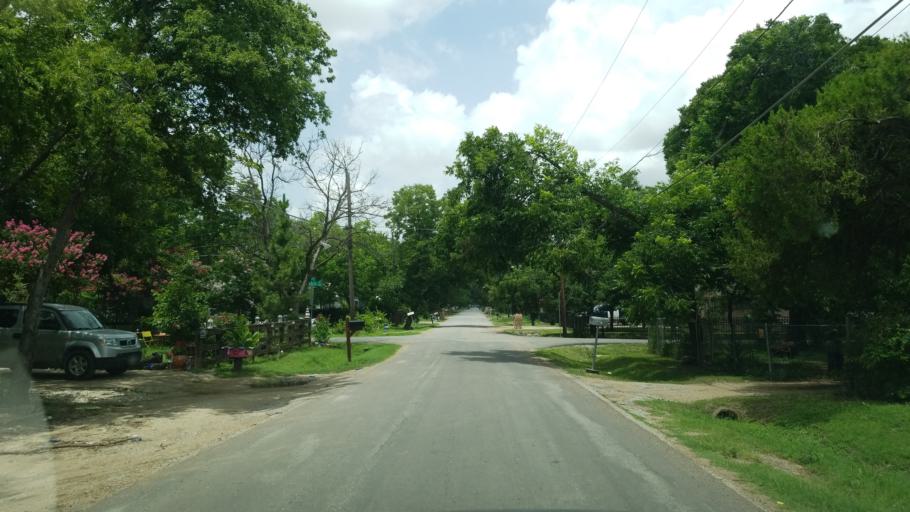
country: US
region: Texas
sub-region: Dallas County
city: Cockrell Hill
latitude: 32.7806
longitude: -96.8989
